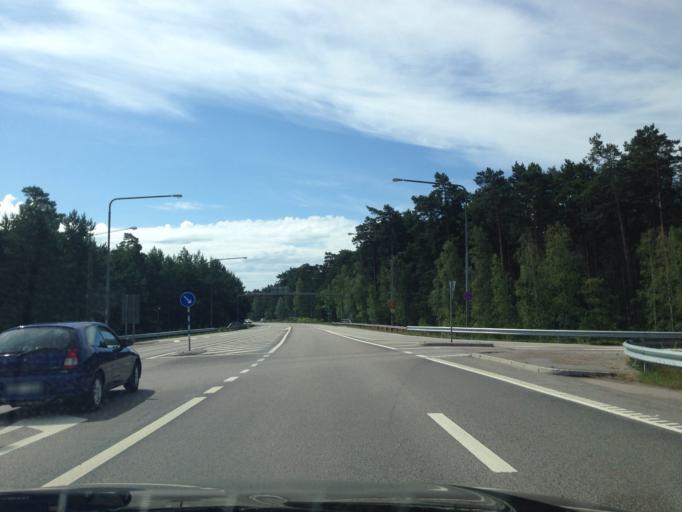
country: SE
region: Kalmar
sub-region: Kalmar Kommun
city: Kalmar
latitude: 56.6845
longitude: 16.3556
